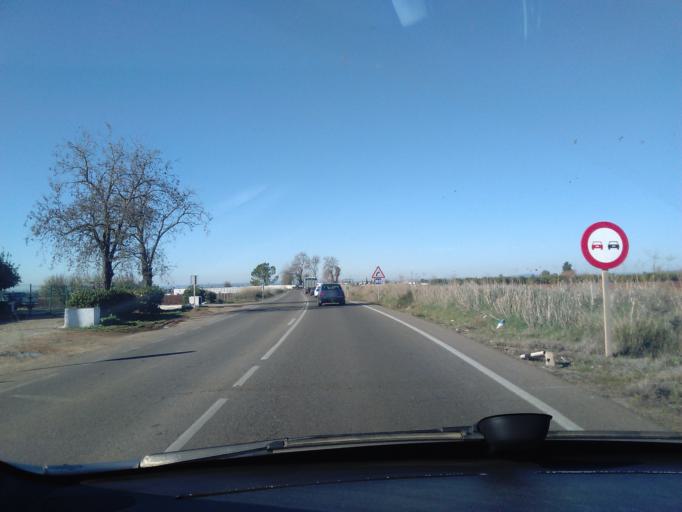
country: ES
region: Andalusia
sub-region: Provincia de Sevilla
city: Sevilla
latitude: 37.4360
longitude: -5.9384
